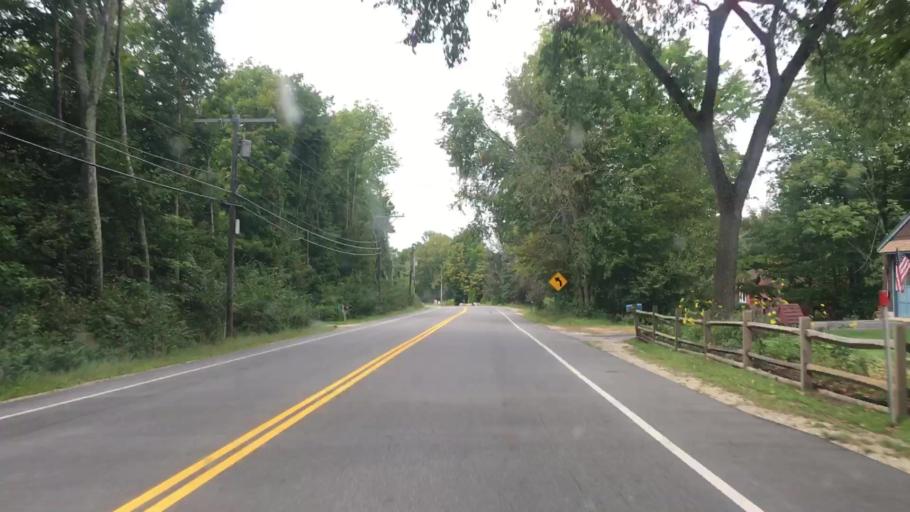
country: US
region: New Hampshire
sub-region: Strafford County
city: Madbury
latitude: 43.2005
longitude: -70.9578
